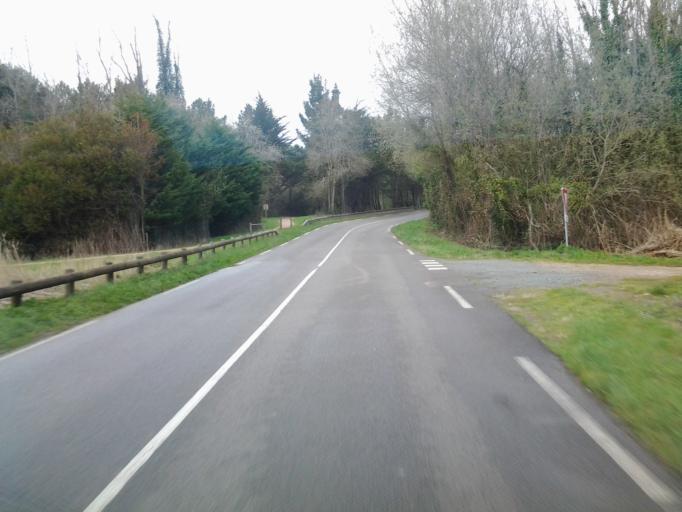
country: FR
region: Pays de la Loire
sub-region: Departement de la Vendee
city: La Tranche-sur-Mer
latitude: 46.3798
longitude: -1.4656
